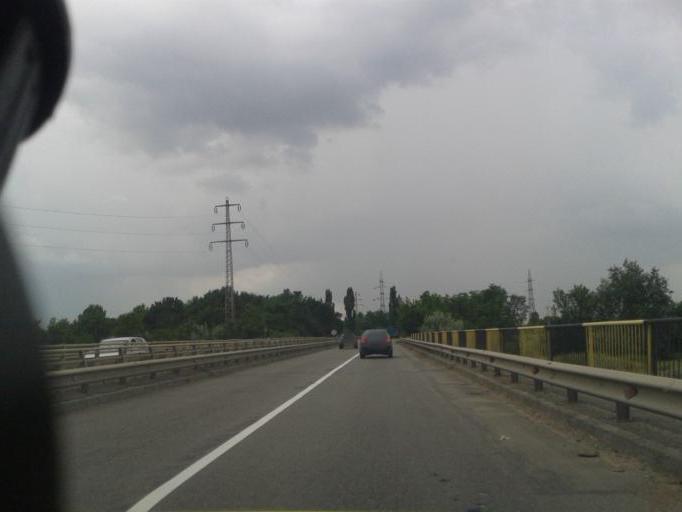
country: RO
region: Prahova
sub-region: Comuna Bucov
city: Bucov
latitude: 44.9645
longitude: 26.0614
